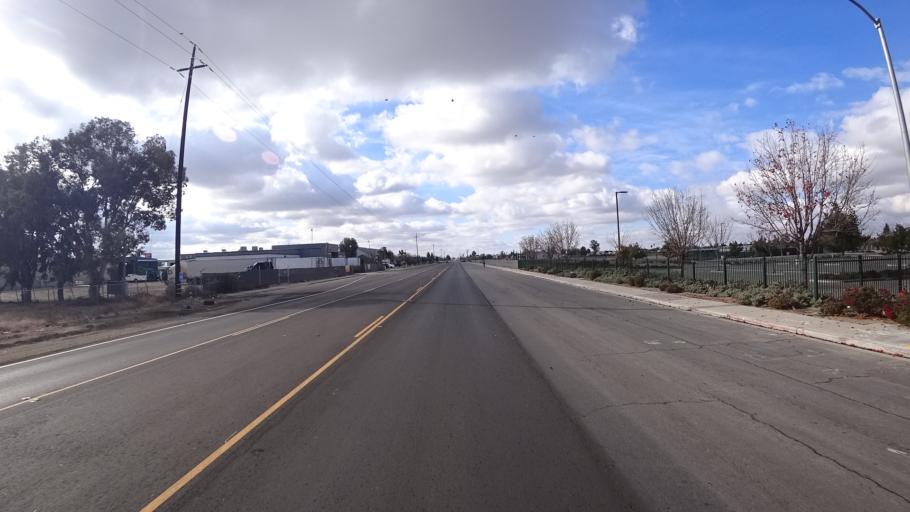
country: US
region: California
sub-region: Kern County
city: Bakersfield
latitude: 35.3542
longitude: -118.9521
